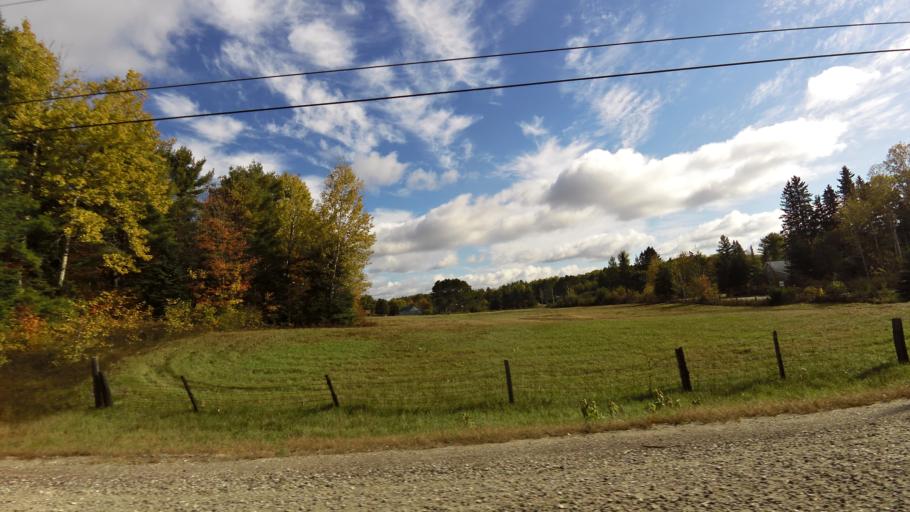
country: CA
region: Ontario
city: Deep River
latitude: 46.0342
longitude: -77.4650
